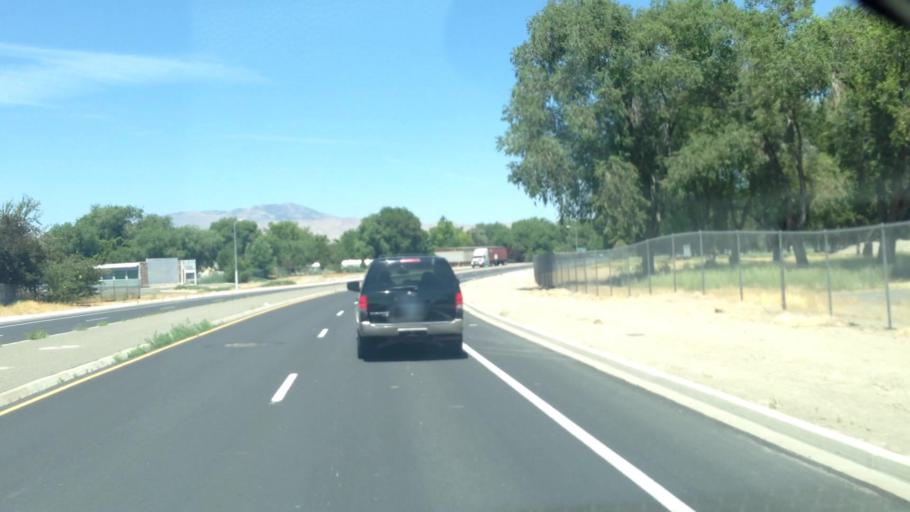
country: US
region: Nevada
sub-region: Washoe County
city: Sparks
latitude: 39.4839
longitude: -119.7743
